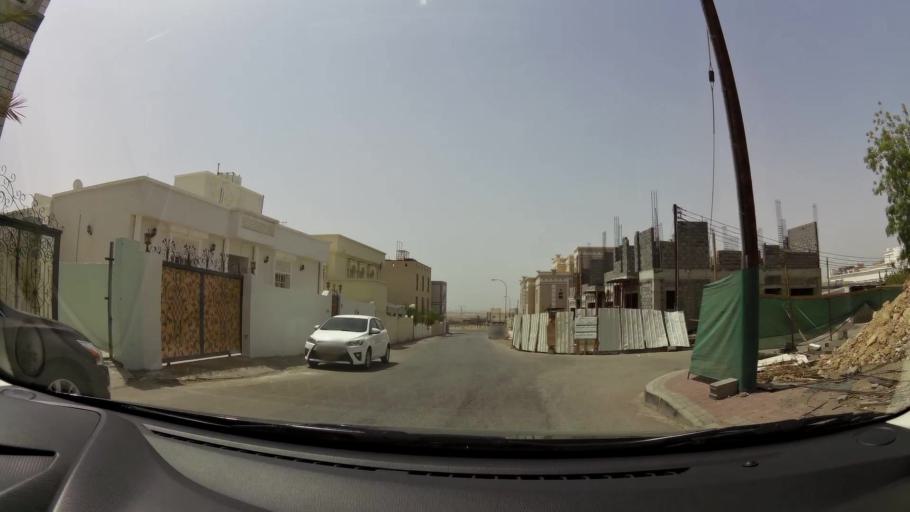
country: OM
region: Muhafazat Masqat
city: Bawshar
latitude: 23.5351
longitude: 58.3836
